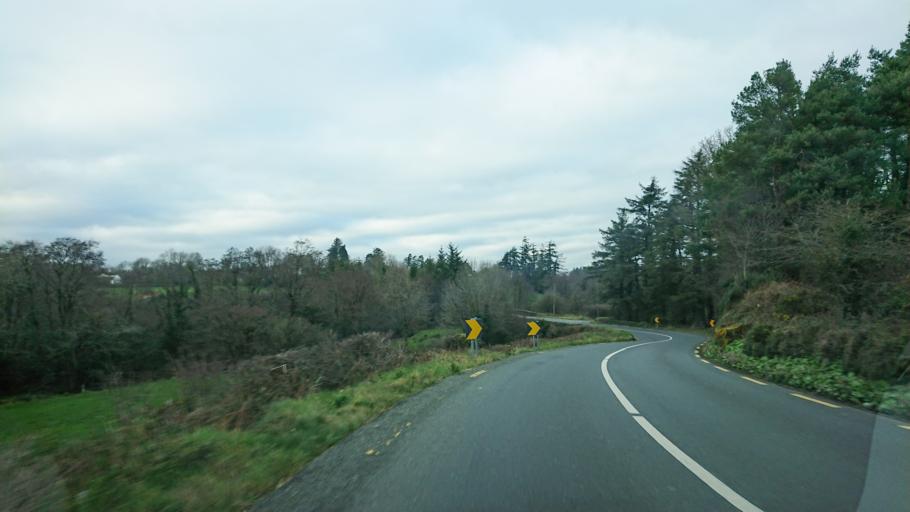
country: IE
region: Munster
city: Carrick-on-Suir
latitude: 52.2997
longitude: -7.4792
